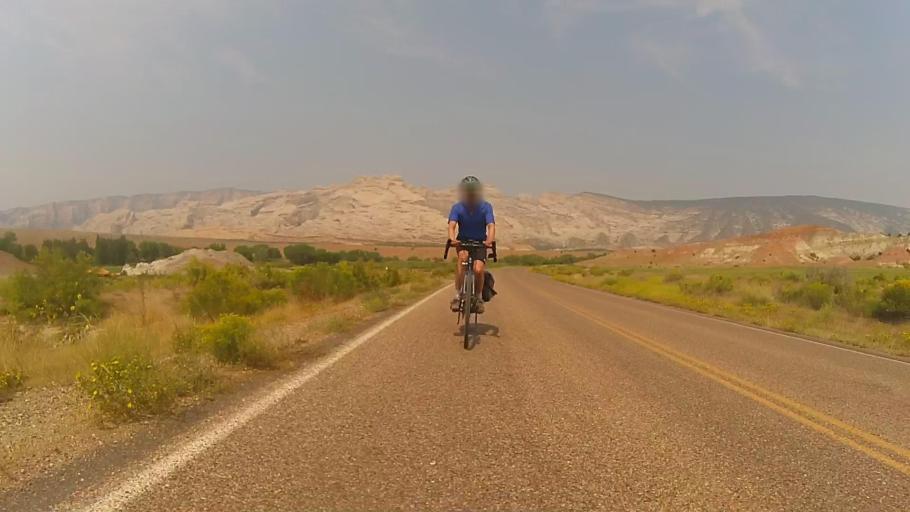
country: US
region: Utah
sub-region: Uintah County
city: Naples
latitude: 40.4198
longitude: -109.2274
